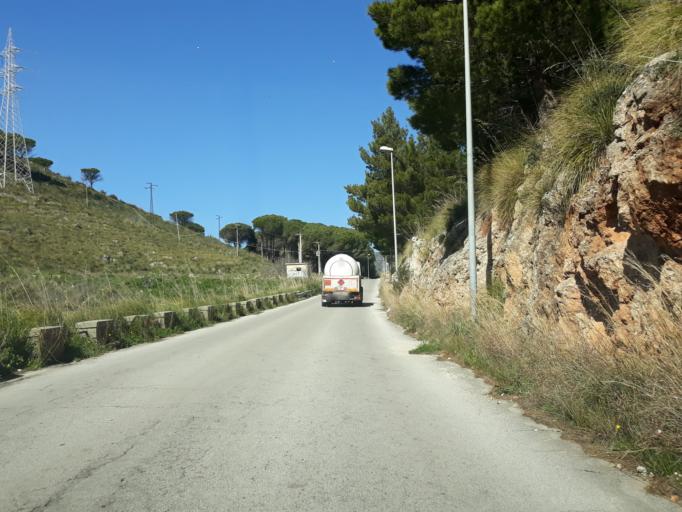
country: IT
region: Sicily
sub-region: Palermo
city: Piano dei Geli
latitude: 38.0811
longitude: 13.2727
